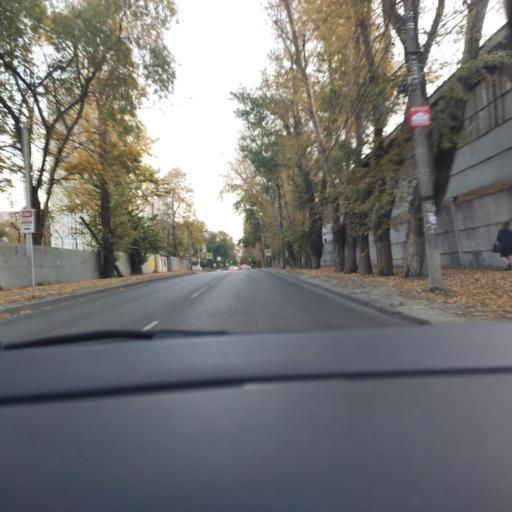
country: RU
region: Voronezj
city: Voronezh
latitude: 51.6893
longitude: 39.1906
